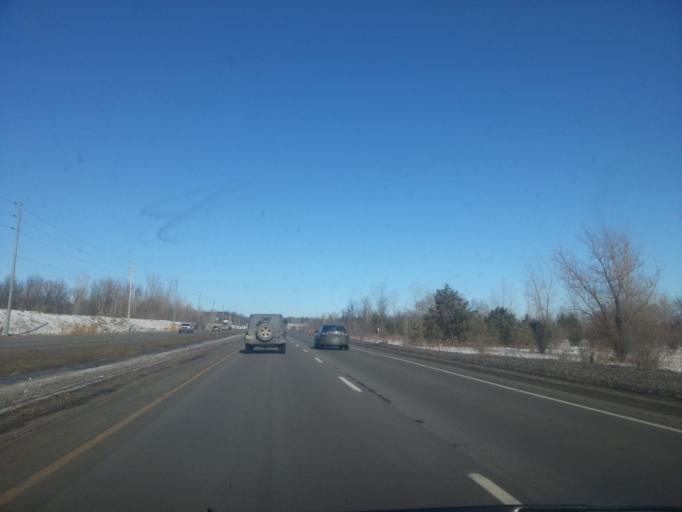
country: CA
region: Ontario
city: Ottawa
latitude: 45.4305
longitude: -75.5548
